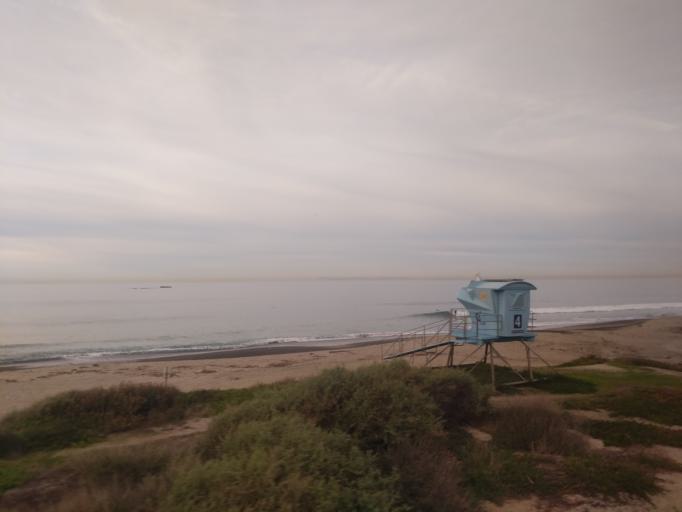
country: US
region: California
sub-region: Orange County
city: San Clemente
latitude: 33.4080
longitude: -117.6090
